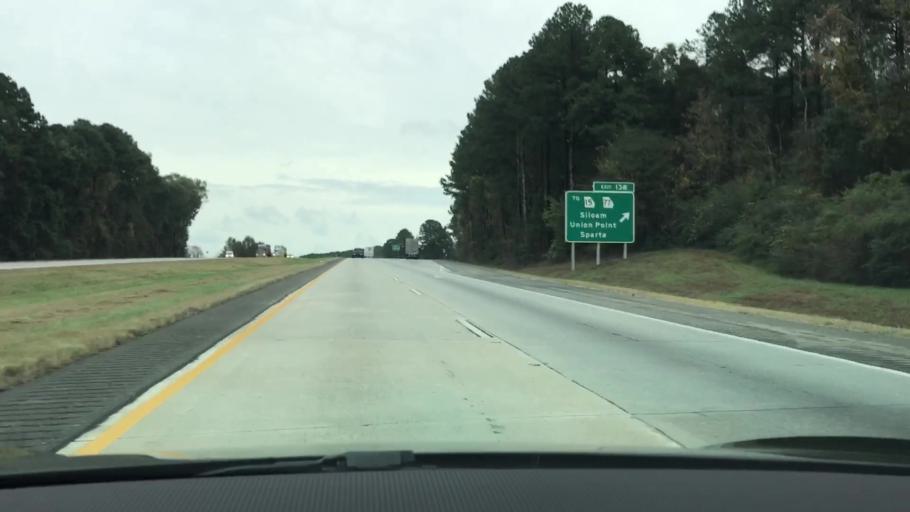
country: US
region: Georgia
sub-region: Greene County
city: Union Point
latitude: 33.5447
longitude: -83.0867
